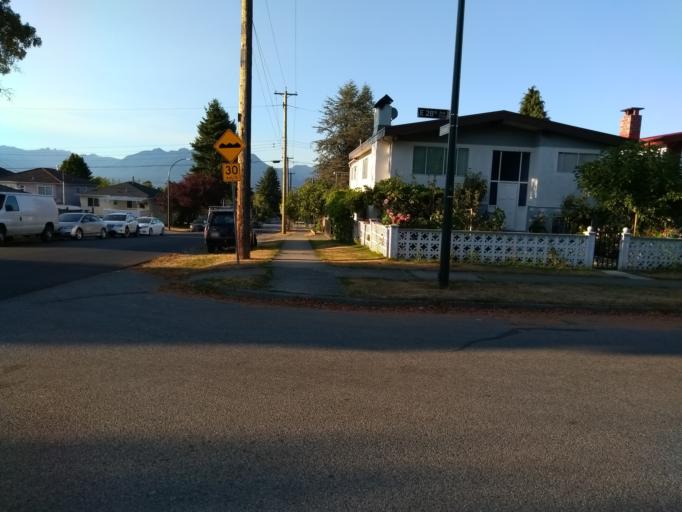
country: CA
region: British Columbia
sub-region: Fraser Valley Regional District
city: North Vancouver
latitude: 49.2453
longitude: -123.0390
